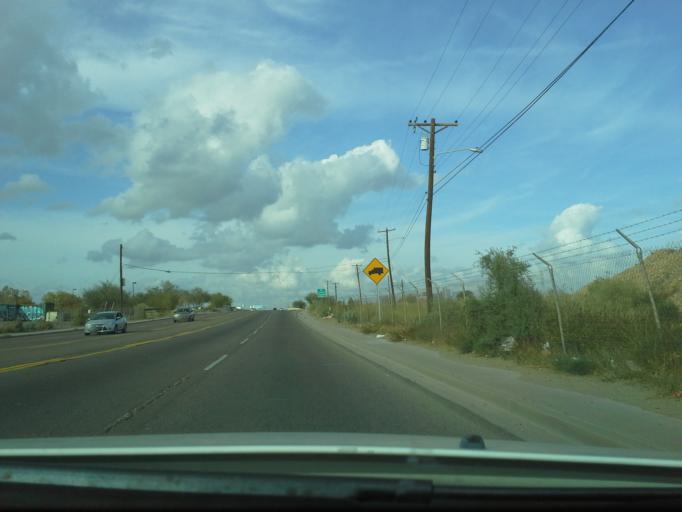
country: US
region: Arizona
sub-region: Maricopa County
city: Phoenix
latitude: 33.4154
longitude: -112.0820
